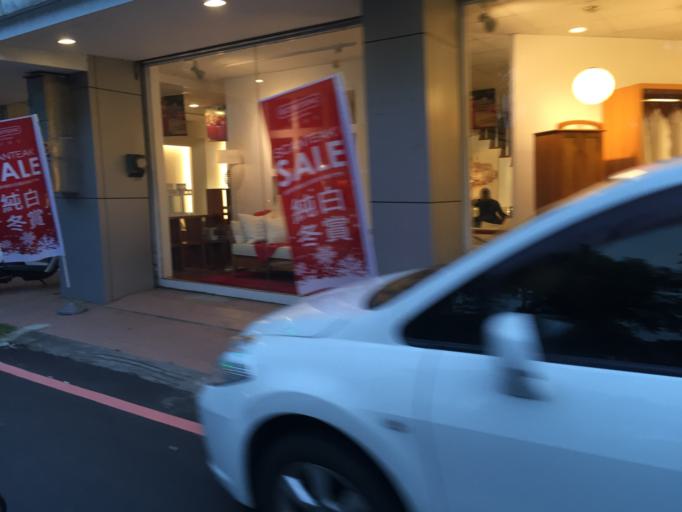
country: TW
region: Taiwan
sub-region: Yilan
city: Yilan
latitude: 24.7641
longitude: 121.7546
